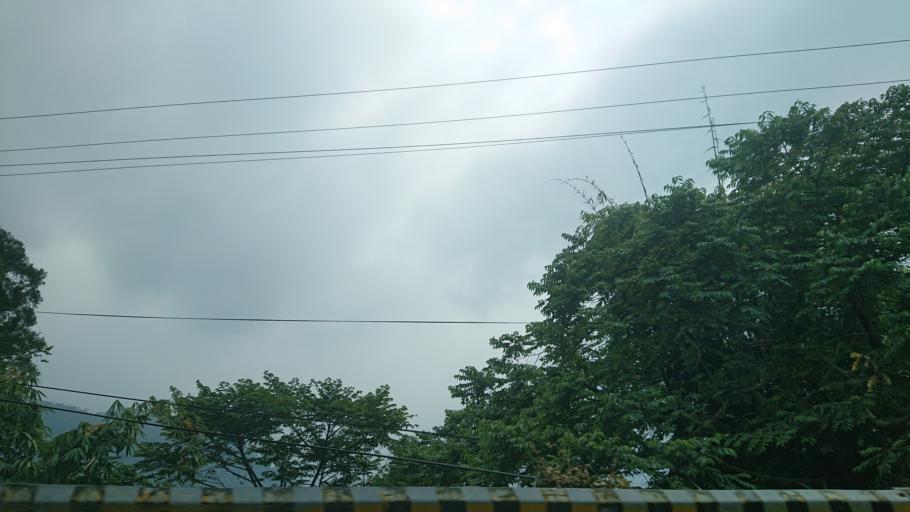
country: TW
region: Taiwan
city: Lugu
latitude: 23.6020
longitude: 120.7024
